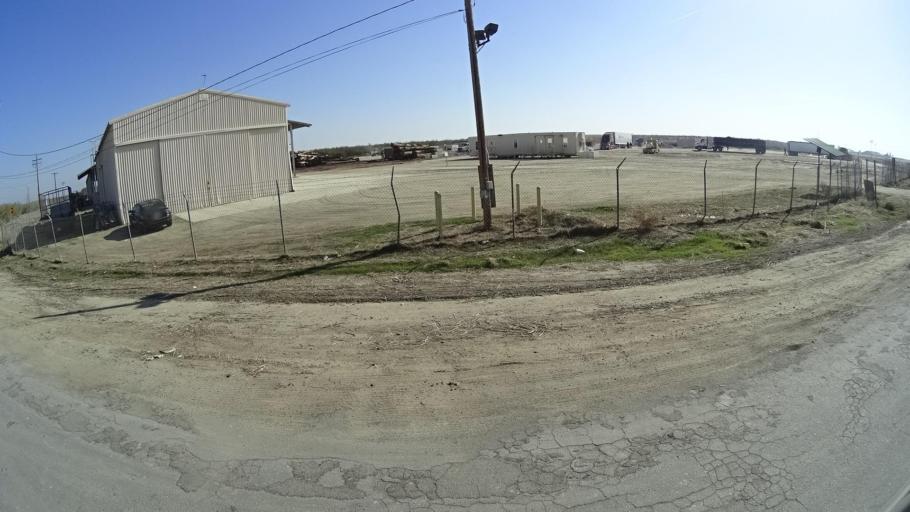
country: US
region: California
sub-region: Kern County
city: McFarland
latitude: 35.6455
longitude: -119.2033
